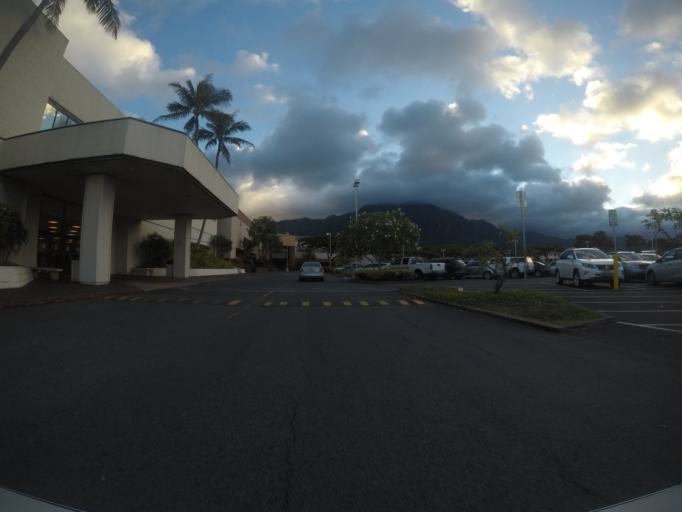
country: US
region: Hawaii
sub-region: Honolulu County
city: He'eia
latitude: 21.4208
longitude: -157.8043
